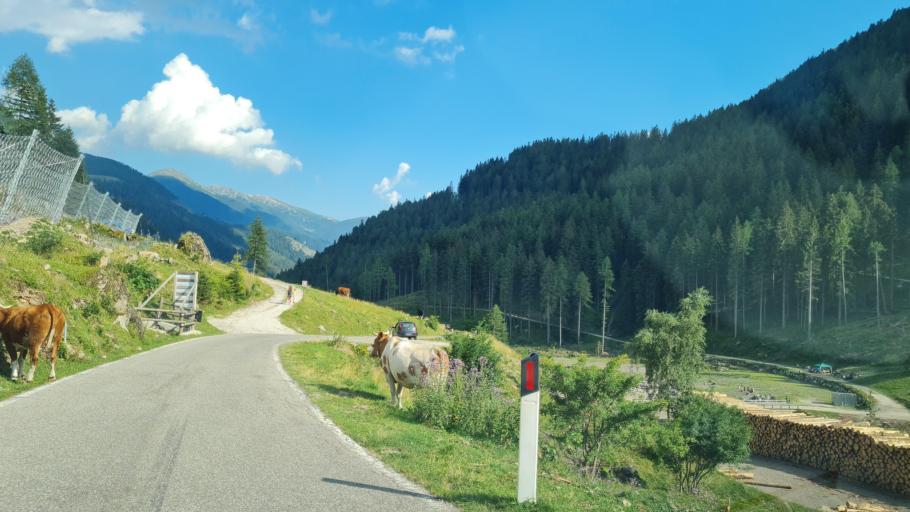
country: IT
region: Trentino-Alto Adige
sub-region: Provincia di Trento
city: Torcegno
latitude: 46.1515
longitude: 11.4455
